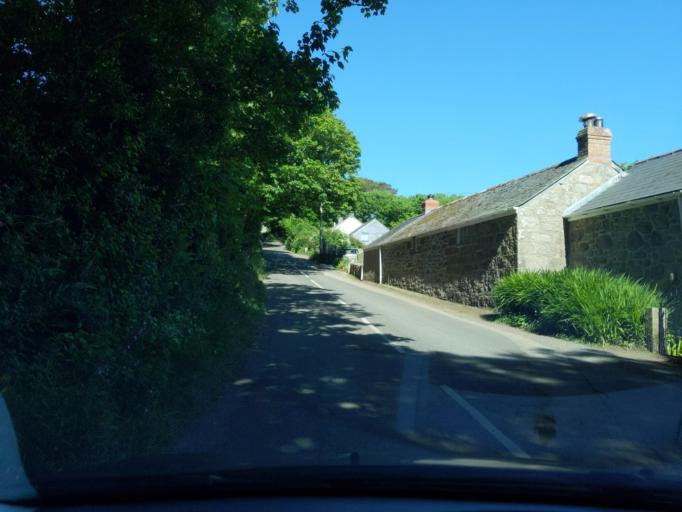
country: GB
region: England
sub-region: Cornwall
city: St. Buryan
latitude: 50.0575
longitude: -5.6230
